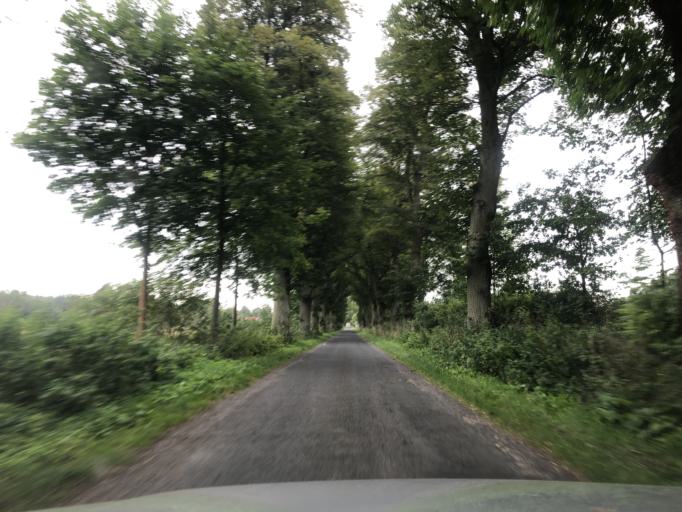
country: PL
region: Greater Poland Voivodeship
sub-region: Powiat pilski
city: Szydlowo
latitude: 53.2705
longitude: 16.6769
